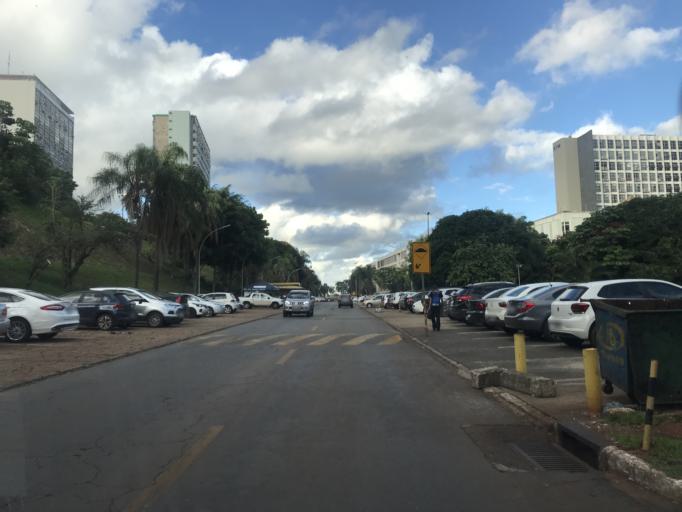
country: BR
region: Federal District
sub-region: Brasilia
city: Brasilia
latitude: -15.8007
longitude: -47.8811
